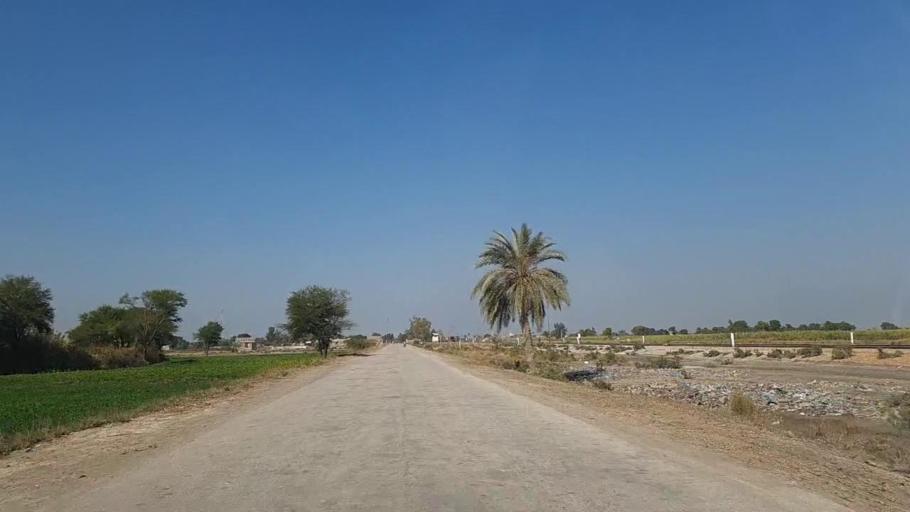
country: PK
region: Sindh
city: Nawabshah
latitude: 26.3447
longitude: 68.3690
